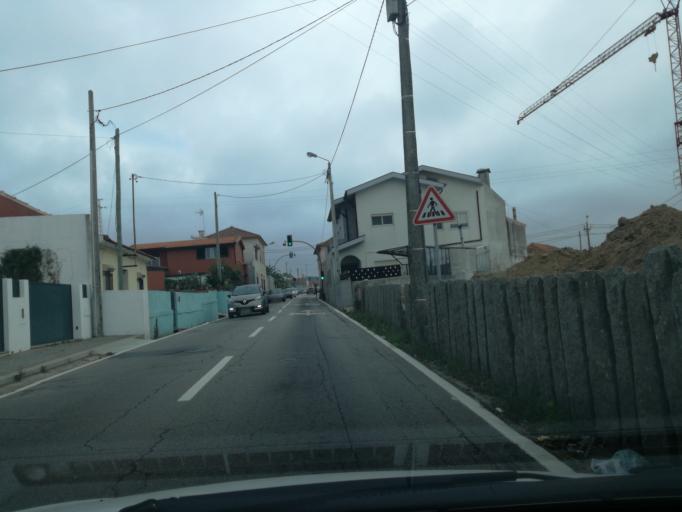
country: PT
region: Aveiro
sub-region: Espinho
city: Silvalde
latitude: 40.9965
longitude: -8.6344
